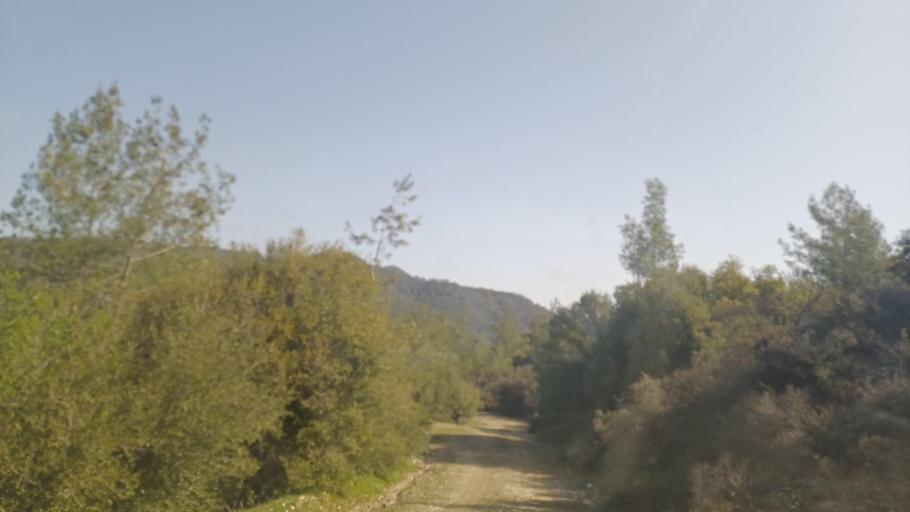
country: CY
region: Limassol
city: Pachna
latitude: 34.8893
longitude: 32.7243
